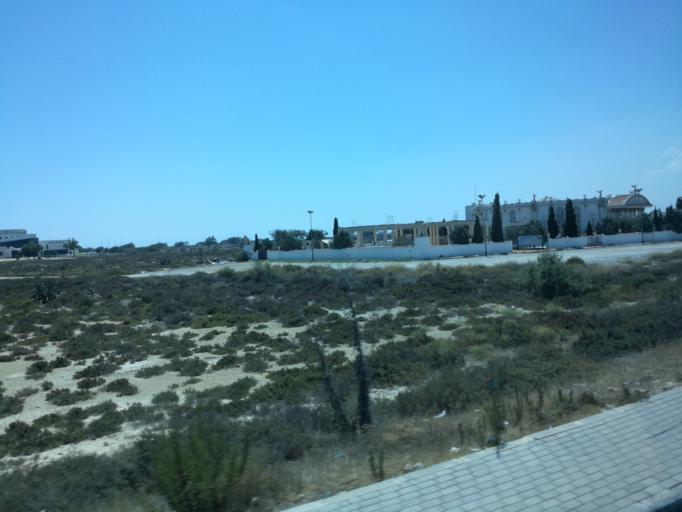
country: CY
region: Ammochostos
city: Famagusta
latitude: 35.1648
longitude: 33.9001
